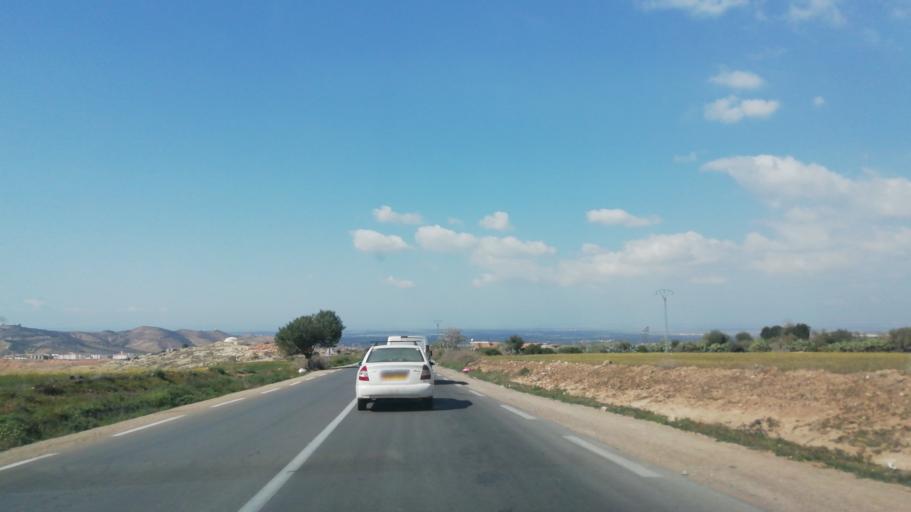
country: DZ
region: Mascara
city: Mascara
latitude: 35.5506
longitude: 0.0851
